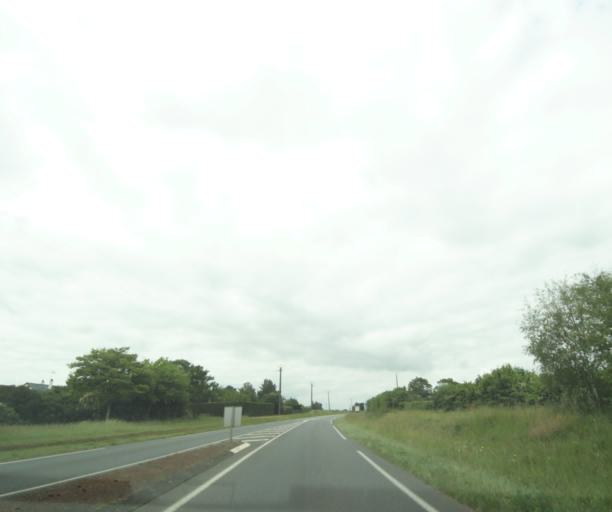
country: FR
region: Pays de la Loire
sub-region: Departement de Maine-et-Loire
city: Montreuil-Bellay
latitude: 47.1424
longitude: -0.1542
